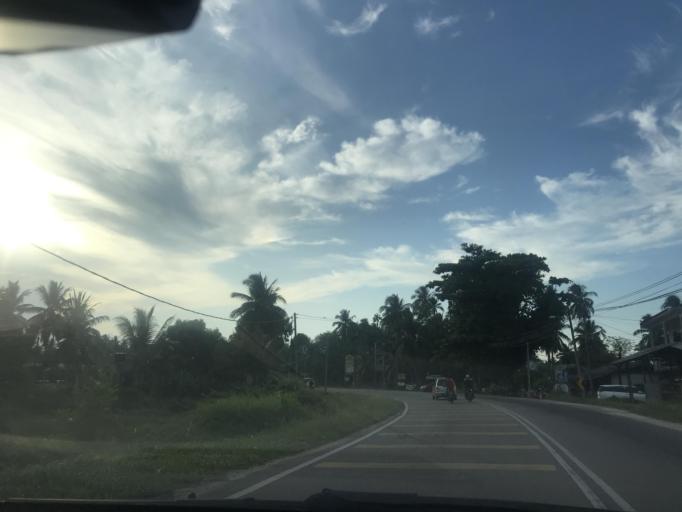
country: MY
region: Kelantan
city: Peringat
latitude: 6.1252
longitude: 102.3563
